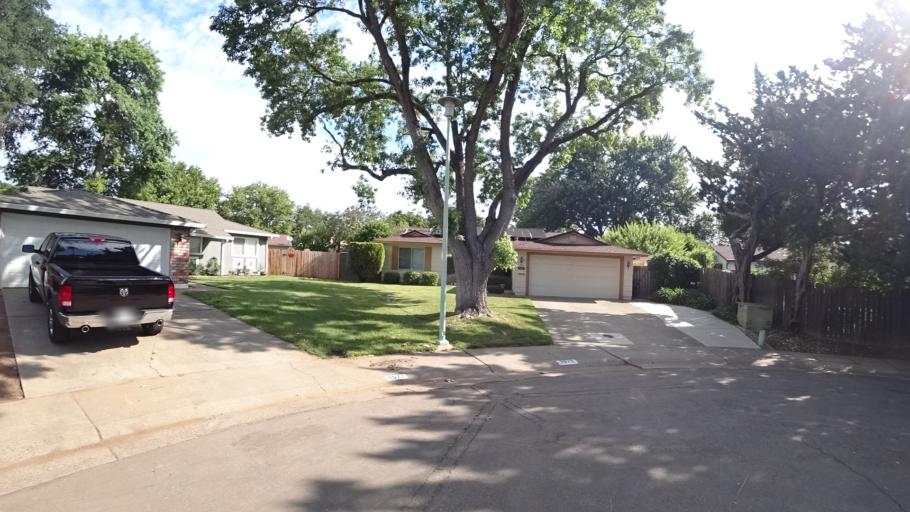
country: US
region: California
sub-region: Sacramento County
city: Rosemont
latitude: 38.5628
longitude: -121.3879
